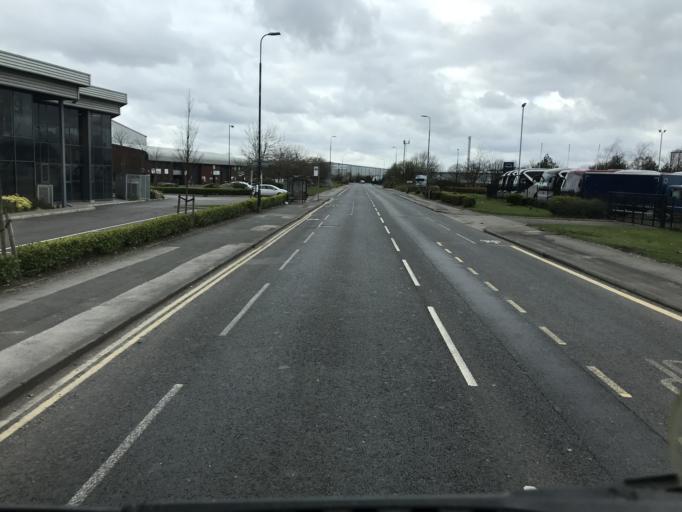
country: GB
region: England
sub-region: City and Borough of Salford
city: Eccles
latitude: 53.4721
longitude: -2.3315
